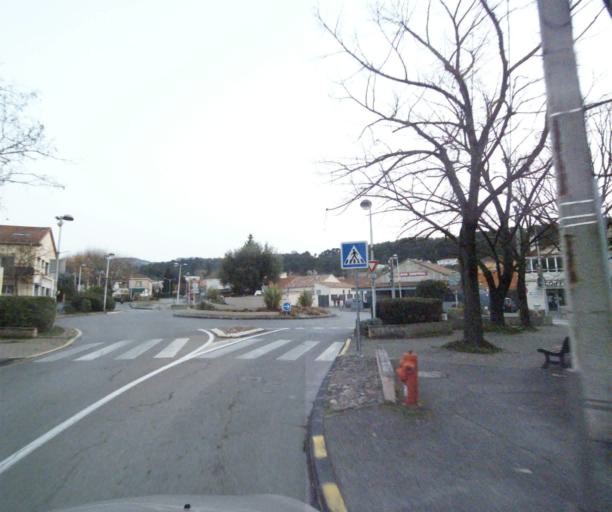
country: FR
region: Provence-Alpes-Cote d'Azur
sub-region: Departement des Bouches-du-Rhone
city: Gardanne
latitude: 43.4343
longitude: 5.4661
